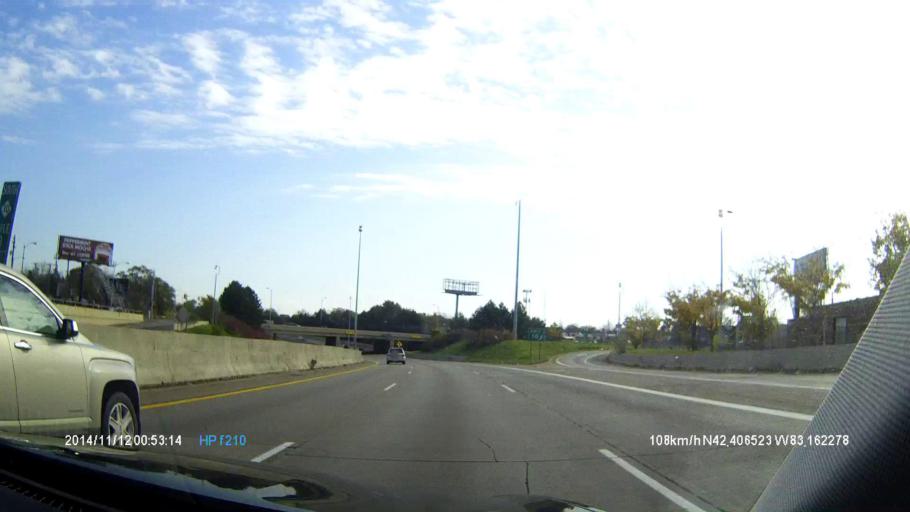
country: US
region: Michigan
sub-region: Oakland County
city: Oak Park
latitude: 42.4064
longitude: -83.1621
